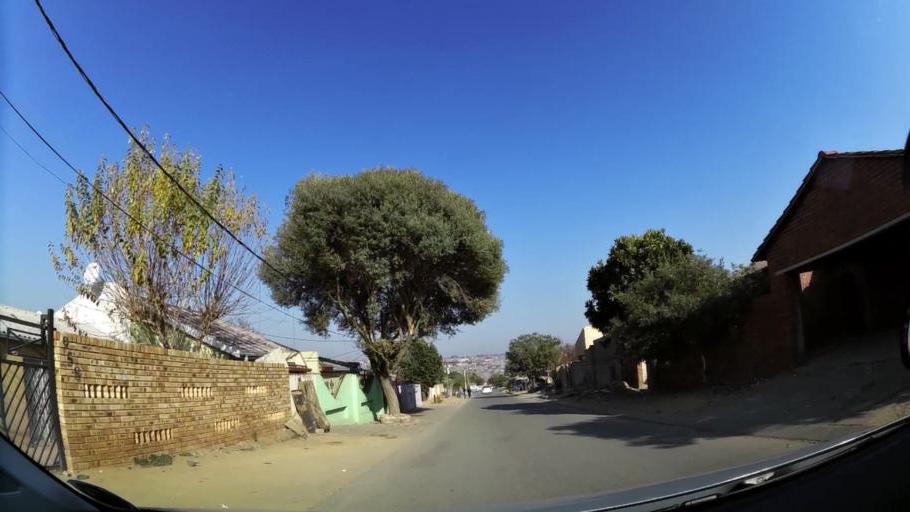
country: ZA
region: Gauteng
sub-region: City of Johannesburg Metropolitan Municipality
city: Modderfontein
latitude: -26.0985
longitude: 28.1180
